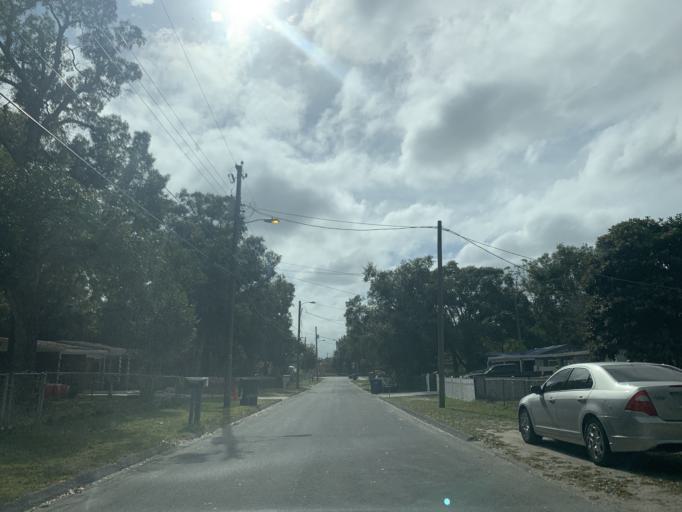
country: US
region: Florida
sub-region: Hillsborough County
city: East Lake-Orient Park
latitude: 27.9755
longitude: -82.3986
